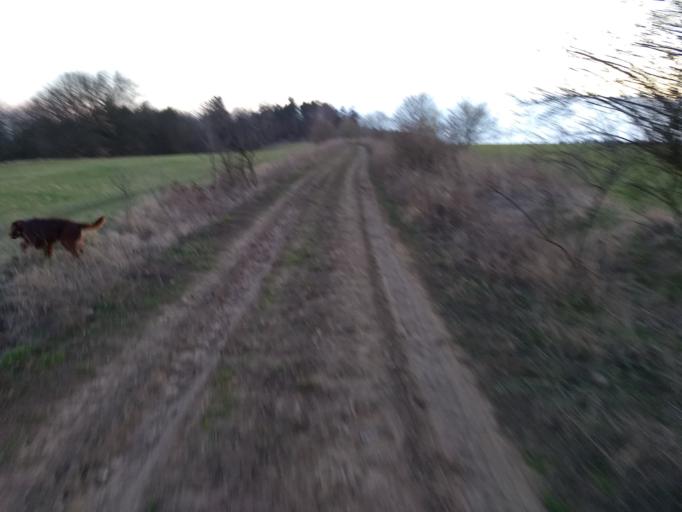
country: CZ
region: Central Bohemia
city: Unhost'
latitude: 50.0472
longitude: 14.1602
